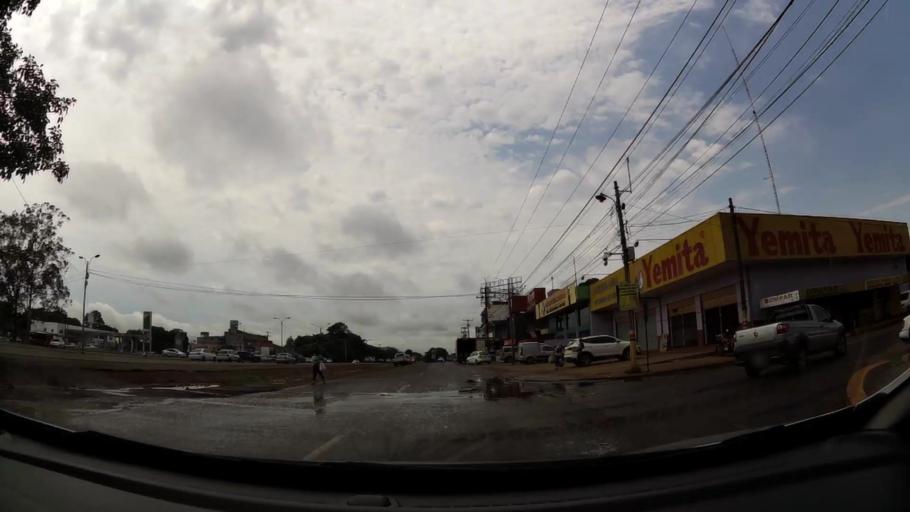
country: PY
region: Alto Parana
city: Ciudad del Este
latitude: -25.4988
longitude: -54.6643
